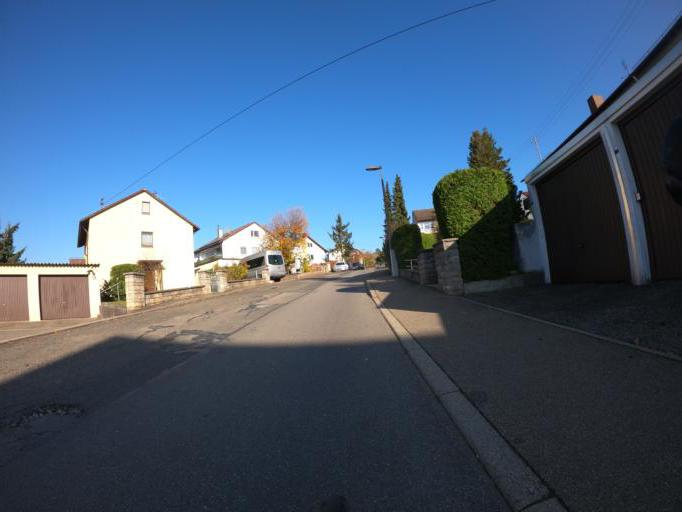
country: DE
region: Baden-Wuerttemberg
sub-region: Regierungsbezirk Stuttgart
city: Aidlingen
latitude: 48.7173
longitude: 8.9049
